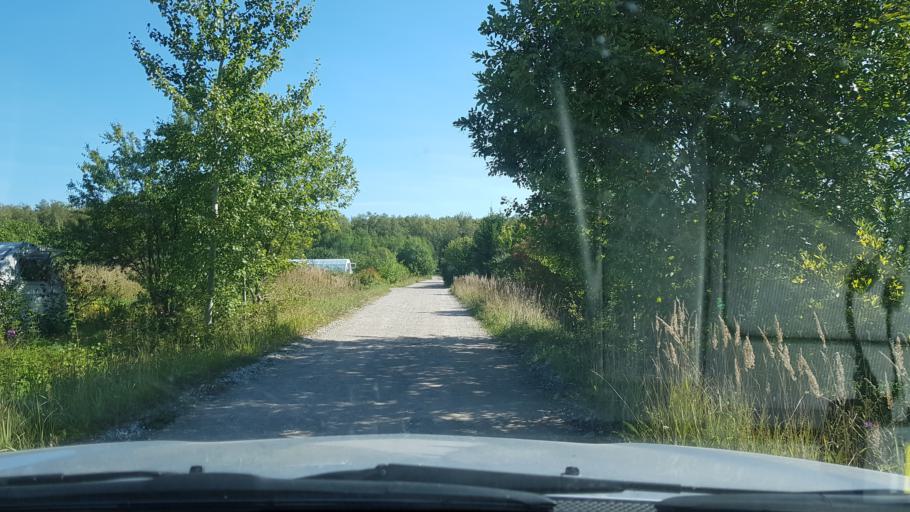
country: EE
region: Ida-Virumaa
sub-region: Sillamaee linn
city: Sillamae
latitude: 59.3716
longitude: 27.7943
